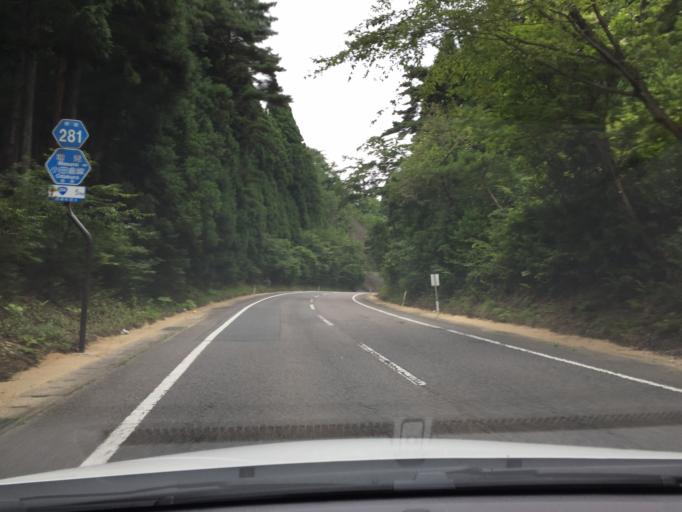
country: JP
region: Fukushima
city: Sukagawa
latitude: 37.1760
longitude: 140.1751
